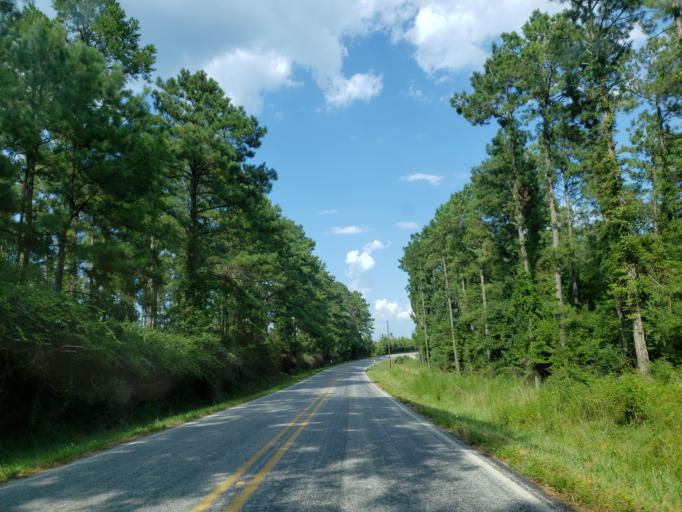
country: US
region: Mississippi
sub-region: Jones County
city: Ellisville
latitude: 31.6224
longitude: -89.3728
